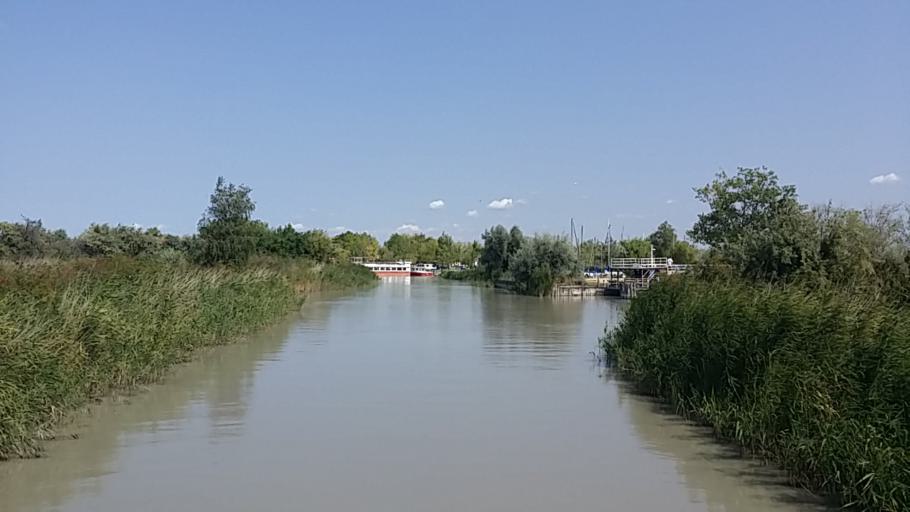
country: AT
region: Burgenland
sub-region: Politischer Bezirk Neusiedl am See
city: Illmitz
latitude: 47.7514
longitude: 16.7402
